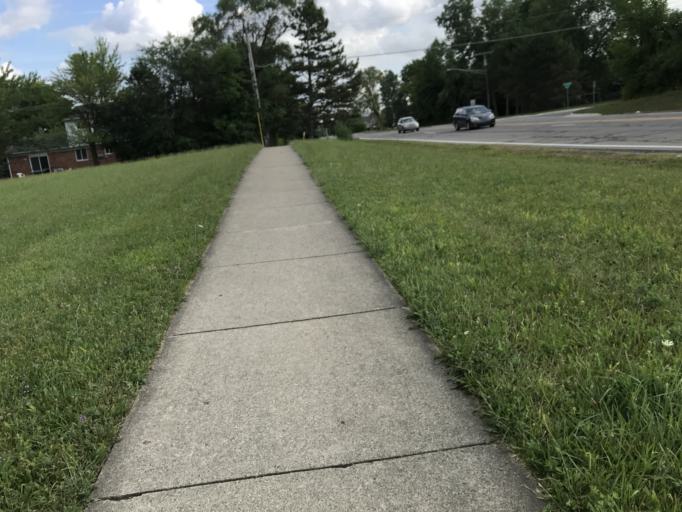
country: US
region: Michigan
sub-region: Oakland County
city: Farmington Hills
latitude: 42.4765
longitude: -83.3378
